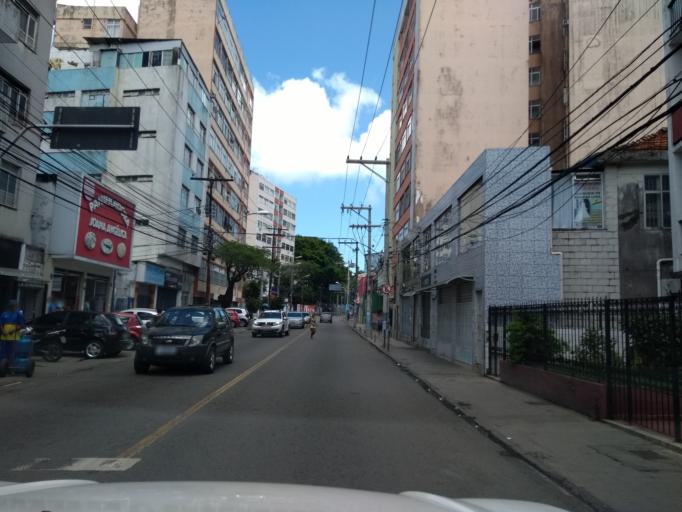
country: BR
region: Bahia
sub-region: Salvador
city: Salvador
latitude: -12.9803
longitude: -38.5091
